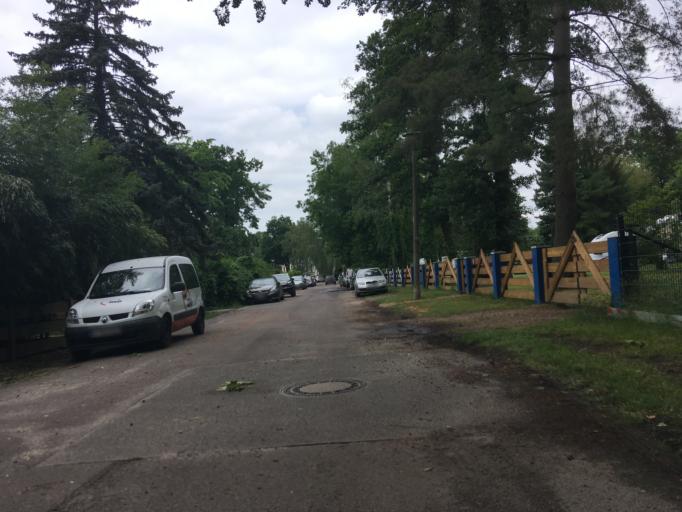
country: DE
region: Berlin
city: Rahnsdorf
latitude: 52.4340
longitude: 13.6873
